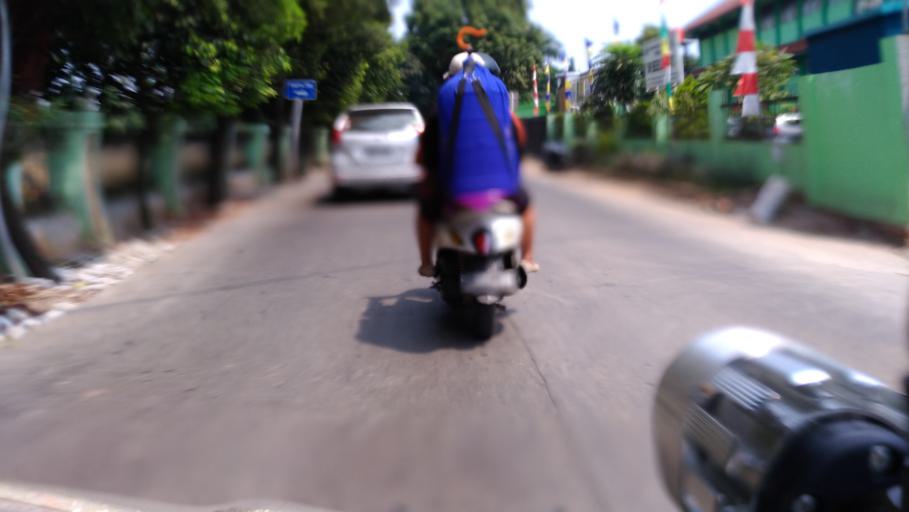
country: ID
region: West Java
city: Cileungsir
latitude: -6.3595
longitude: 106.9090
